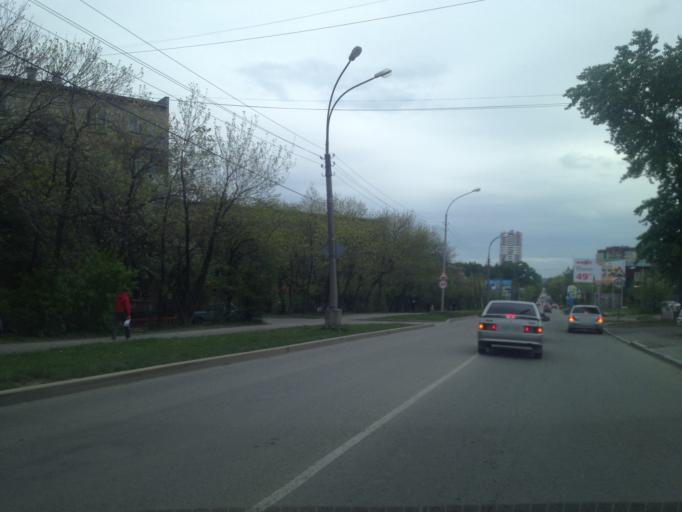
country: RU
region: Sverdlovsk
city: Sovkhoznyy
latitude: 56.7739
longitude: 60.6001
